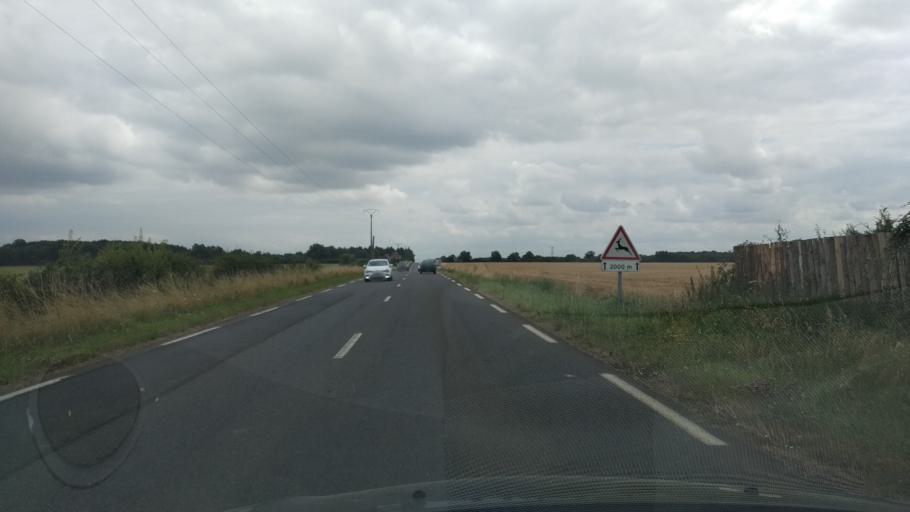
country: FR
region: Poitou-Charentes
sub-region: Departement de la Vienne
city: Saint-Maurice-la-Clouere
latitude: 46.4110
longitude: 0.3883
